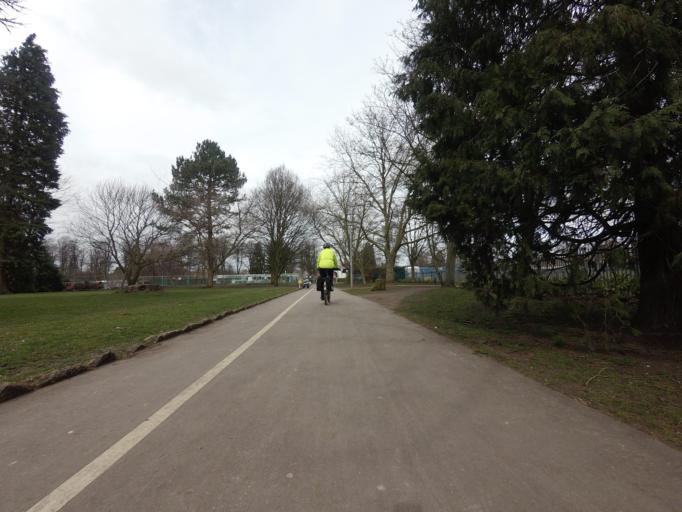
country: GB
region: England
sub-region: Lincolnshire
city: Grantham
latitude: 52.9169
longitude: -0.6371
